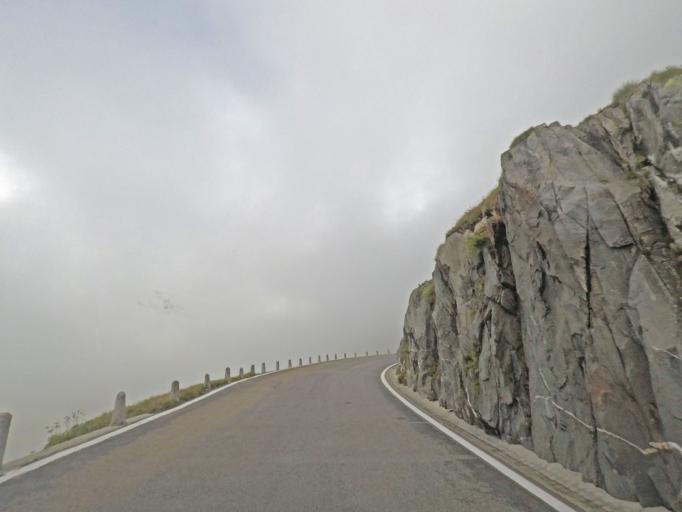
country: CH
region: Uri
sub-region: Uri
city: Andermatt
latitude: 46.5838
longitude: 8.4285
